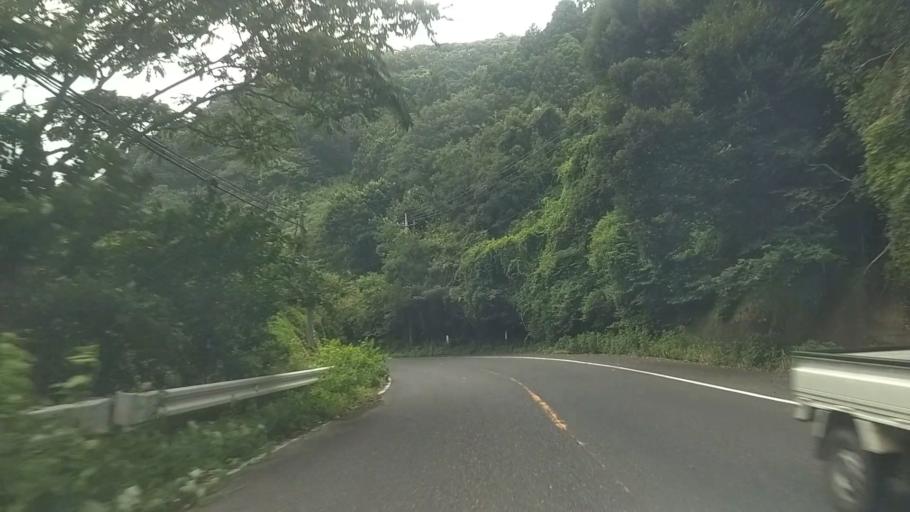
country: JP
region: Chiba
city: Tateyama
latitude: 35.1413
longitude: 139.8987
